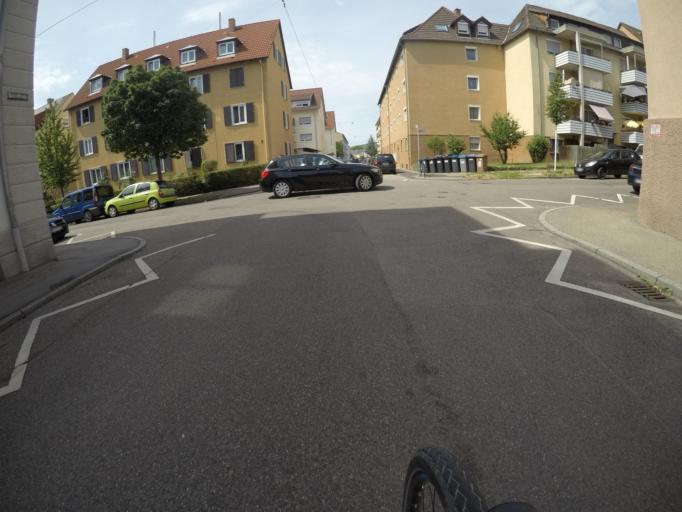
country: DE
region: Baden-Wuerttemberg
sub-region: Regierungsbezirk Stuttgart
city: Esslingen
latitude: 48.7521
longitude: 9.2763
